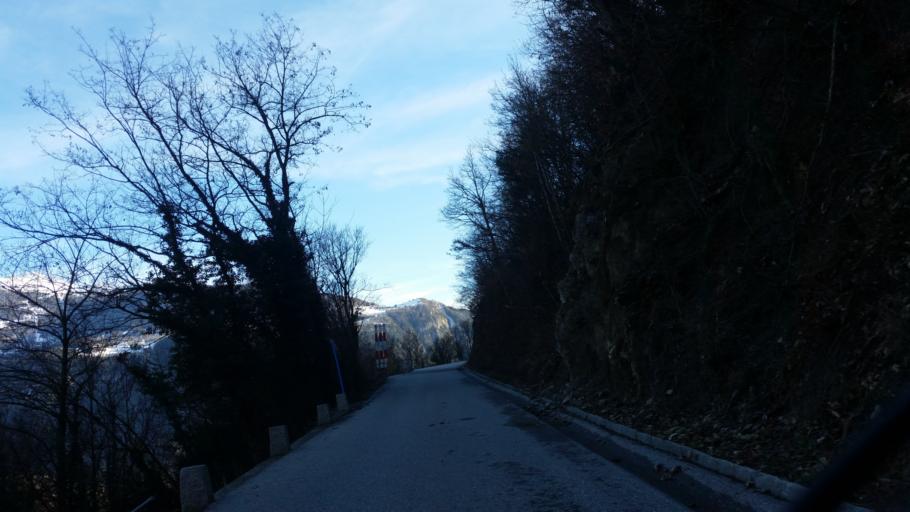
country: CH
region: Valais
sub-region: Sion District
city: Saint-Leonard
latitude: 46.2647
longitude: 7.4071
